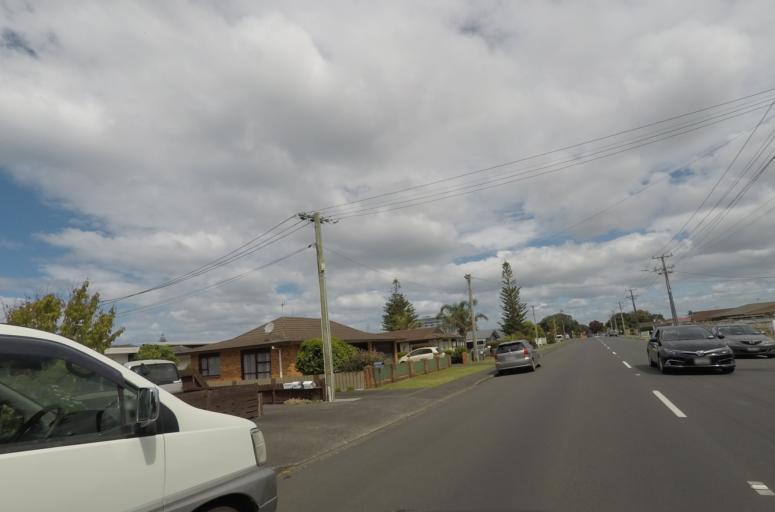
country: NZ
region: Auckland
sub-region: Auckland
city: Rothesay Bay
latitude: -36.5838
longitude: 174.6906
